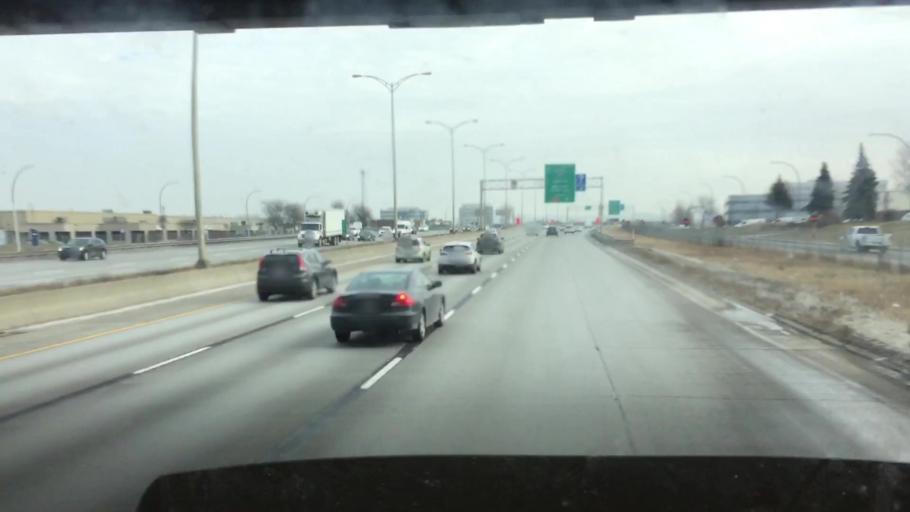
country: CA
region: Quebec
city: Dorval
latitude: 45.4903
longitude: -73.7515
